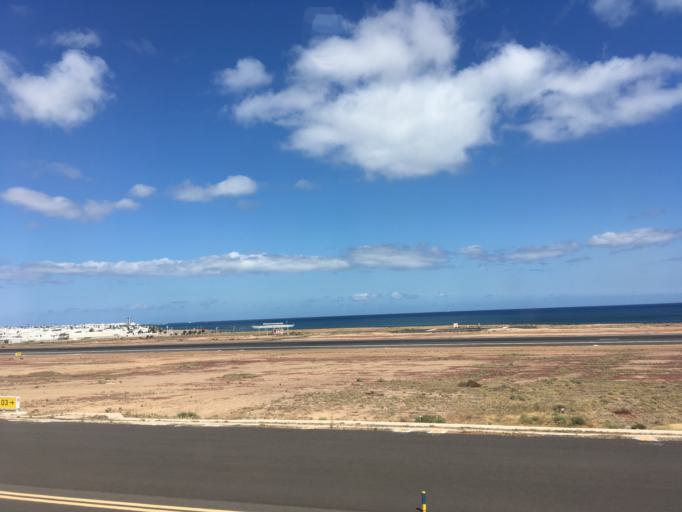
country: ES
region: Canary Islands
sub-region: Provincia de Las Palmas
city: Tias
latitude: 28.9484
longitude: -13.6057
